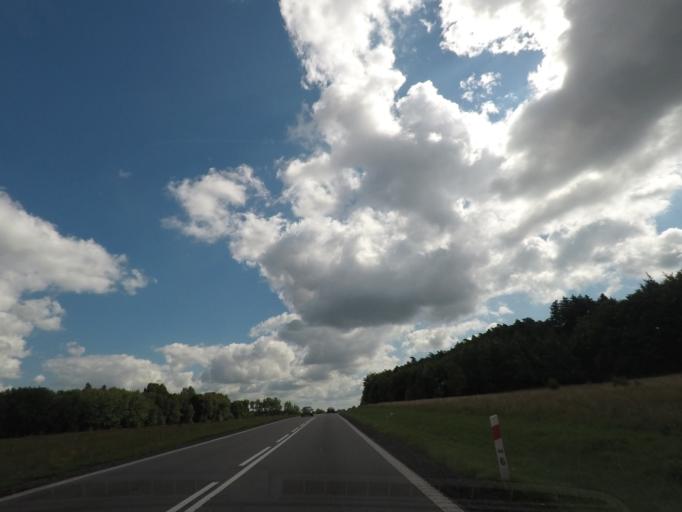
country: PL
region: Pomeranian Voivodeship
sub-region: Powiat wejherowski
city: Leczyce
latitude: 54.5742
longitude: 17.8749
